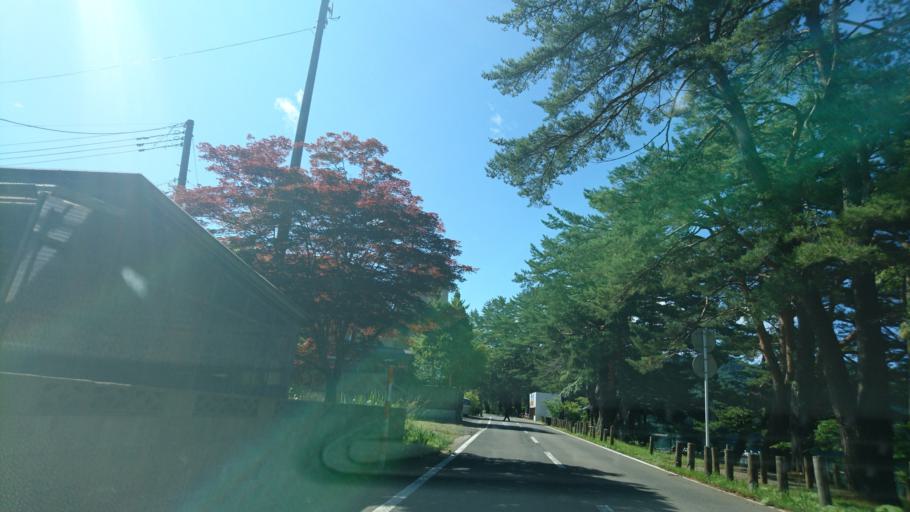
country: JP
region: Akita
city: Kakunodatemachi
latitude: 39.7350
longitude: 140.6970
